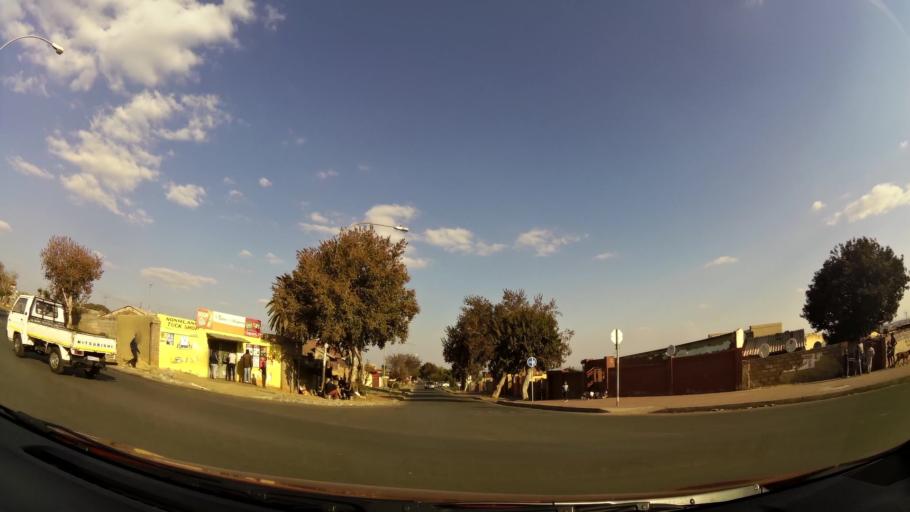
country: ZA
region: Gauteng
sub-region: City of Johannesburg Metropolitan Municipality
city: Roodepoort
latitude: -26.2062
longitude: 27.8840
